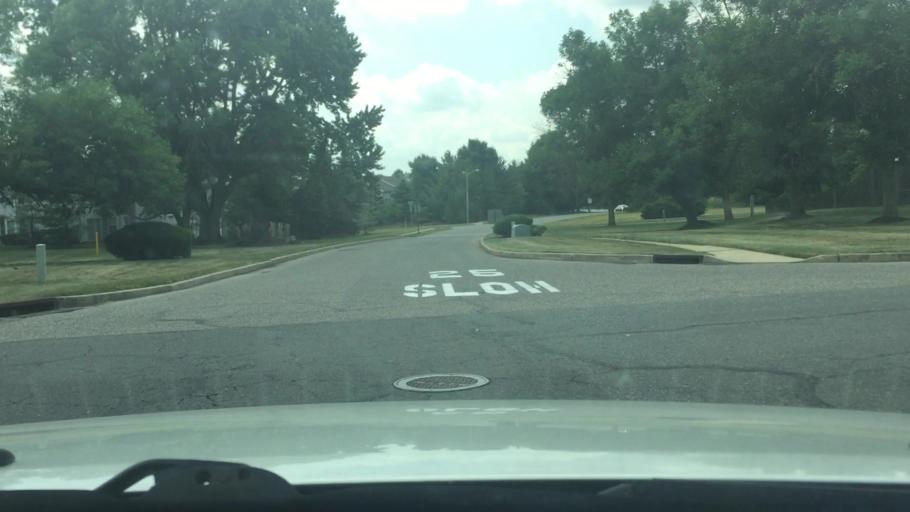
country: US
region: New Jersey
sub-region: Middlesex County
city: East Brunswick
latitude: 40.4259
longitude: -74.4016
